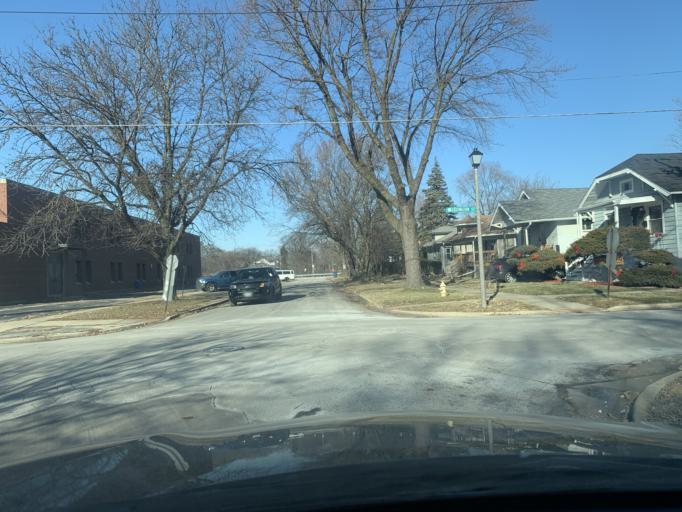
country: US
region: Illinois
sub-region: Cook County
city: Maywood
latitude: 41.8698
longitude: -87.8373
